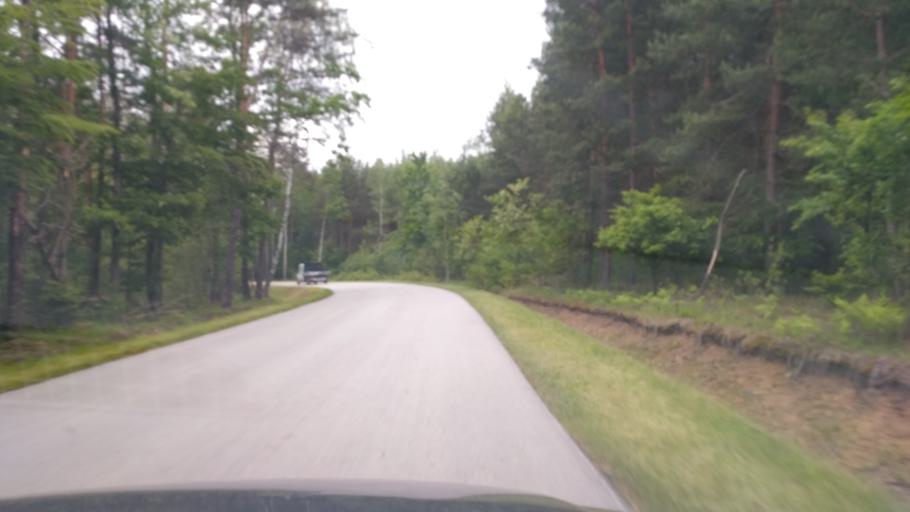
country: PL
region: Subcarpathian Voivodeship
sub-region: Powiat kolbuszowski
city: Niwiska
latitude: 50.2044
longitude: 21.6465
